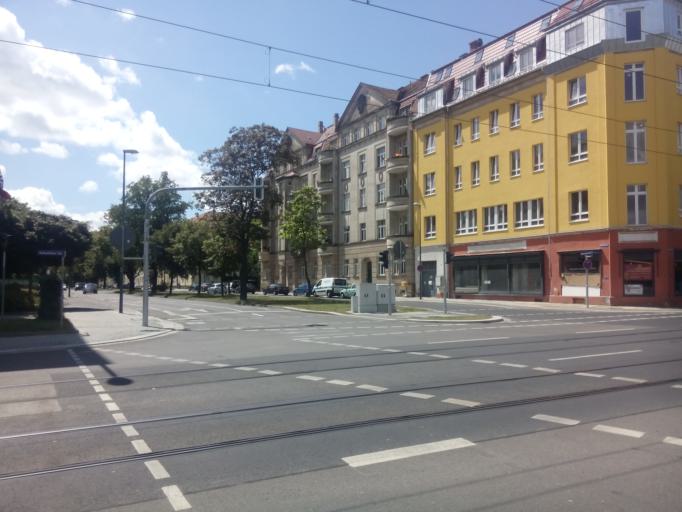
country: DE
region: Saxony
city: Albertstadt
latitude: 51.0434
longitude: 13.7889
